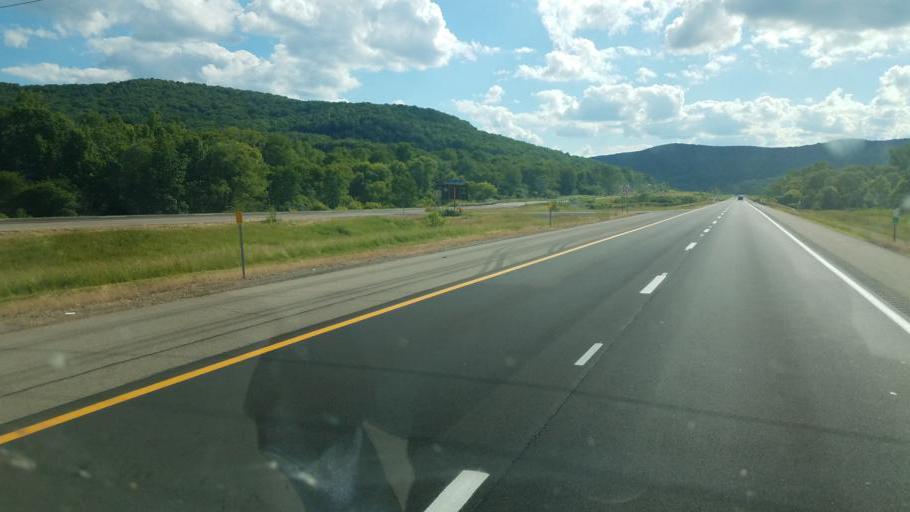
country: US
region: New York
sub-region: Allegany County
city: Cuba
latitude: 42.2172
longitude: -78.3052
